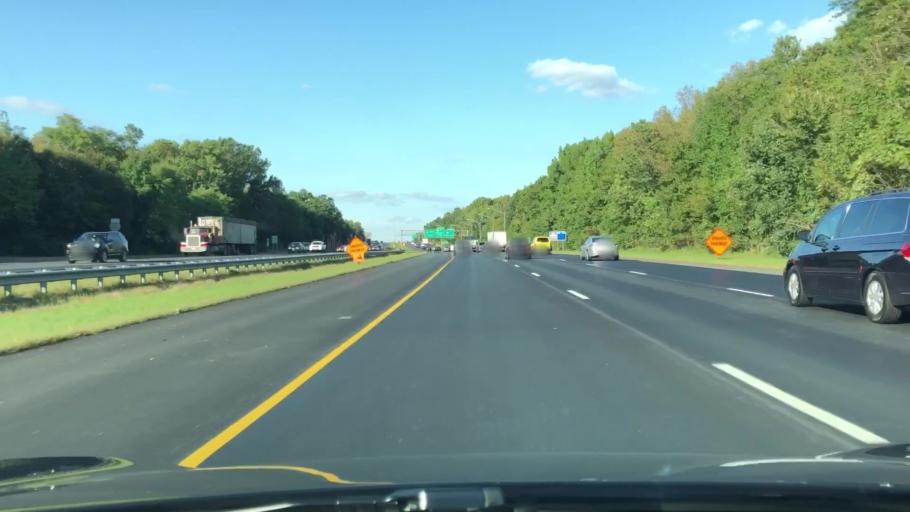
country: US
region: New Jersey
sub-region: Camden County
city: Springdale
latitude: 39.9021
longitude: -74.9874
